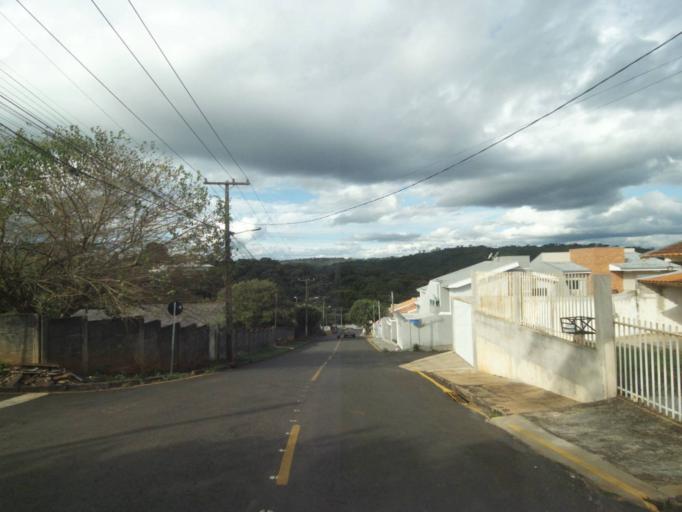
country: BR
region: Parana
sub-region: Telemaco Borba
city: Telemaco Borba
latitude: -24.3377
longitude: -50.6096
